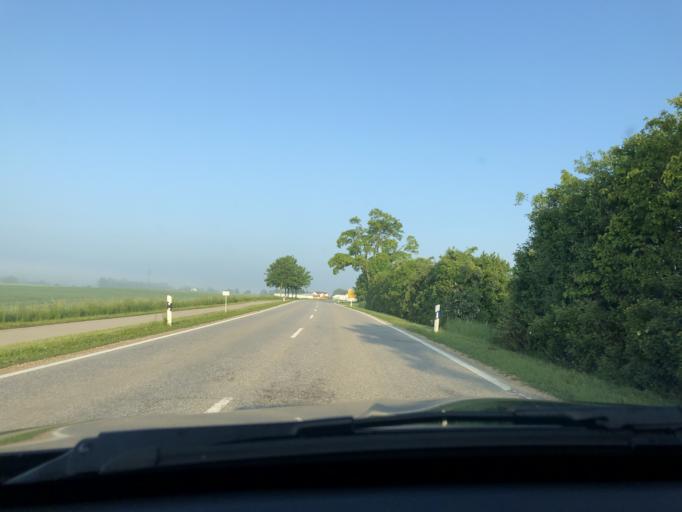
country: DE
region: Bavaria
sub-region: Upper Bavaria
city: Kirchdorf
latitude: 48.4577
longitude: 11.6653
